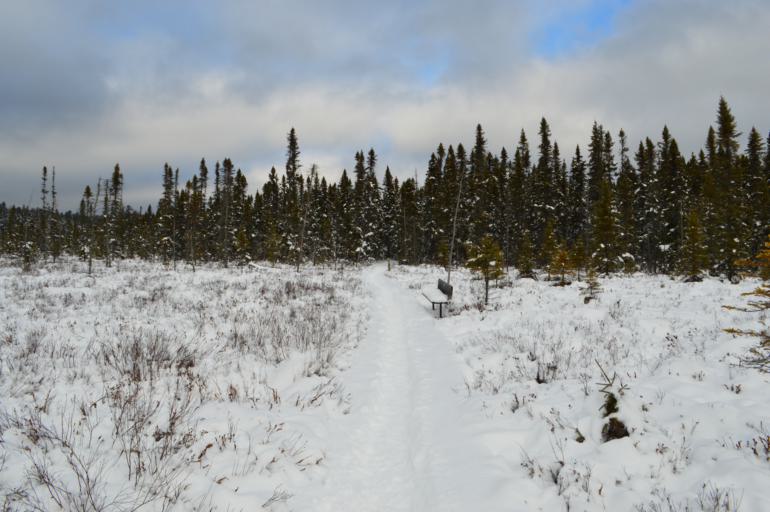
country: CA
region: Ontario
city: Bancroft
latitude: 45.5894
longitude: -78.3724
